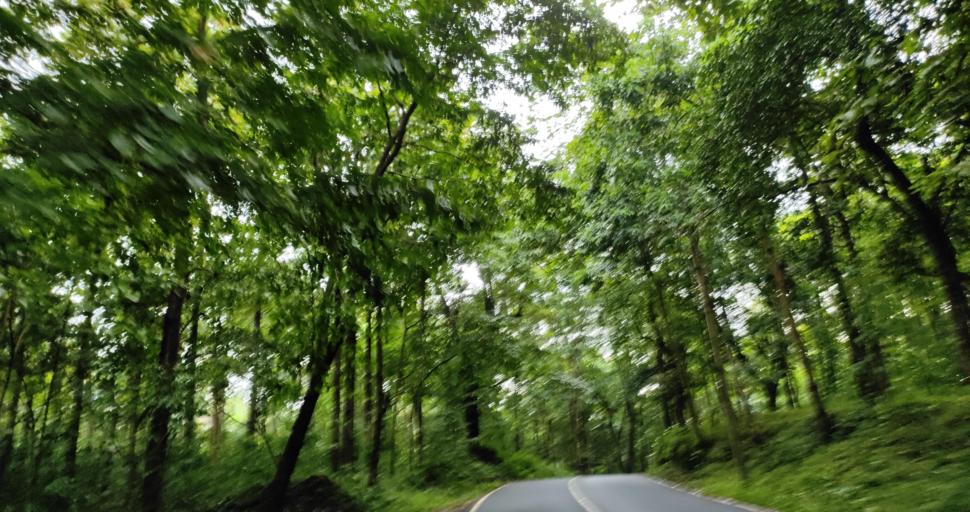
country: IN
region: Kerala
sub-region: Thrissur District
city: Kizhake Chalakudi
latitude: 10.3004
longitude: 76.4428
